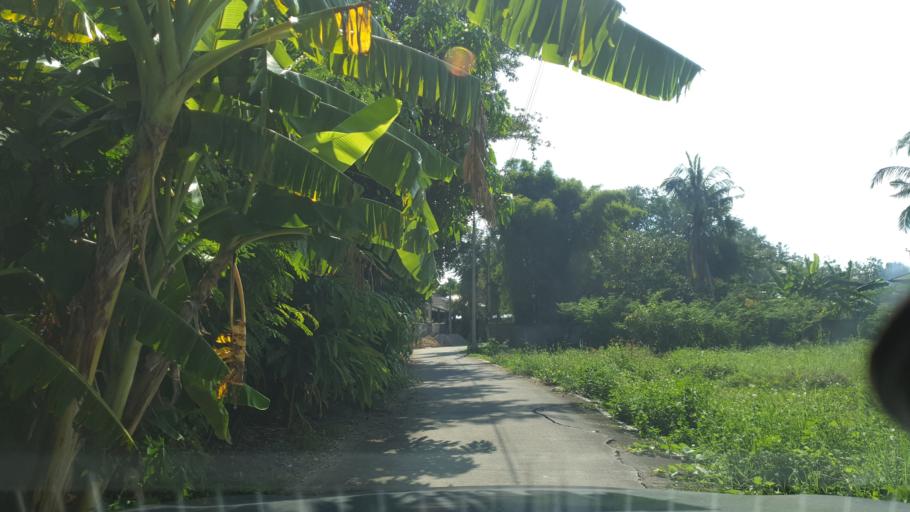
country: TH
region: Chiang Mai
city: Mae Taeng
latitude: 19.0078
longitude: 98.9702
